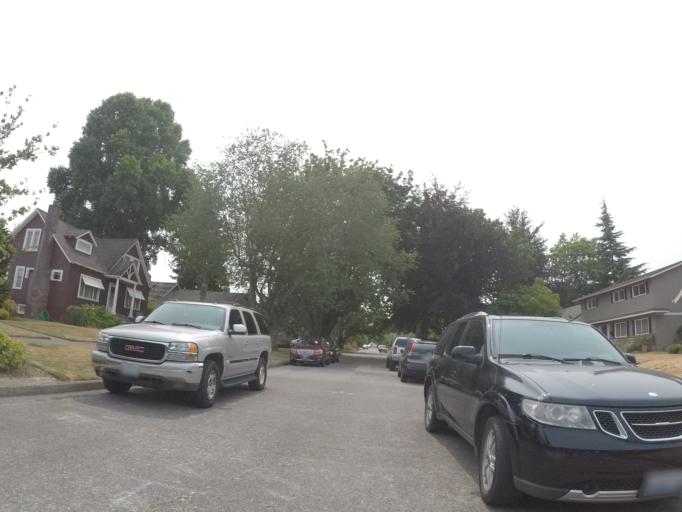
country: US
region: Washington
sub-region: King County
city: Seattle
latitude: 47.5887
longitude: -122.3890
